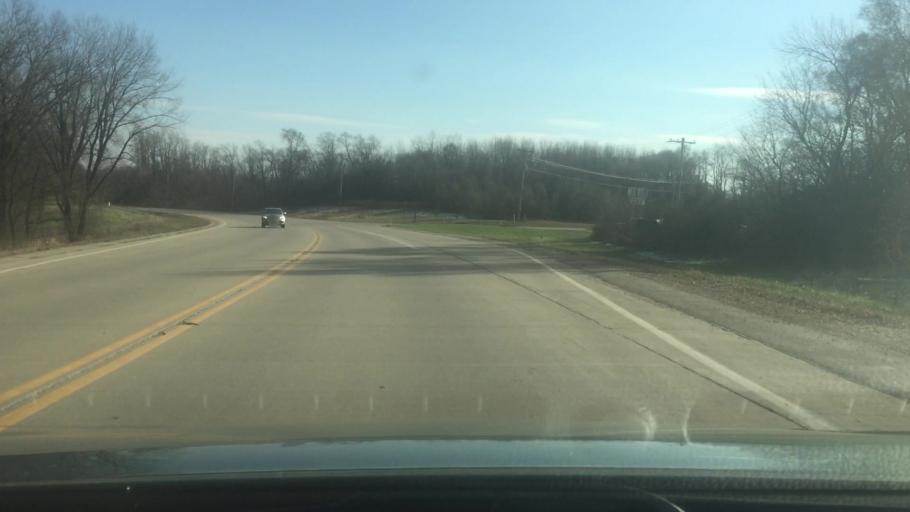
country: US
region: Wisconsin
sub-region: Jefferson County
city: Lake Ripley
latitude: 42.9926
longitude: -88.9990
